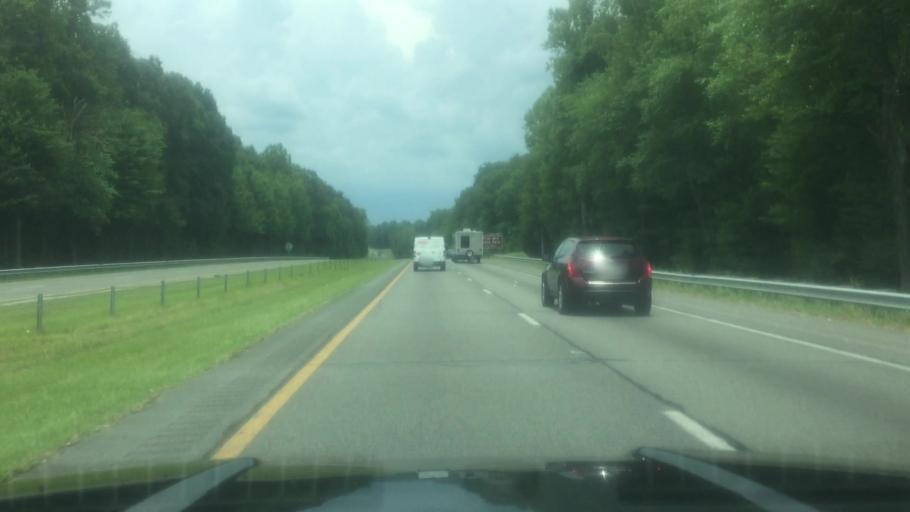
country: US
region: North Carolina
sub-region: Surry County
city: Pilot Mountain
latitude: 36.3303
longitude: -80.4521
